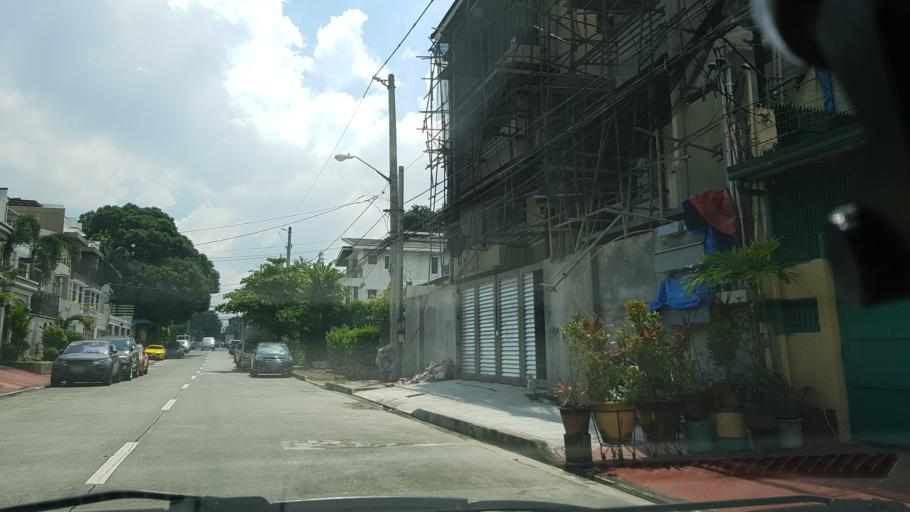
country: PH
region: Calabarzon
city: Del Monte
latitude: 14.6329
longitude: 121.0289
